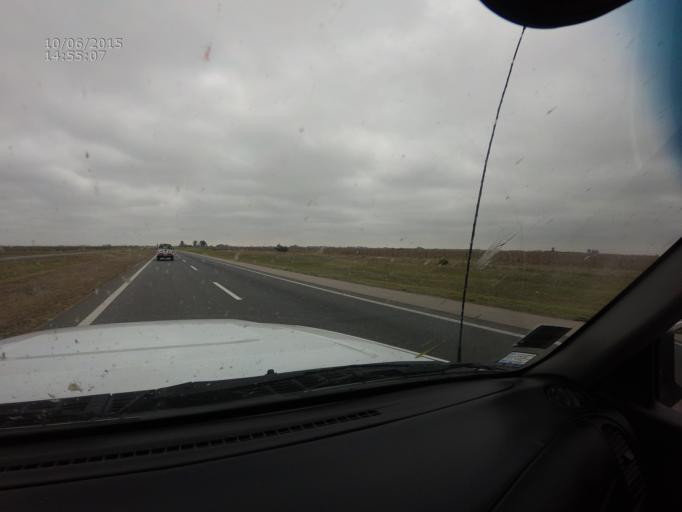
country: AR
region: Cordoba
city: Oncativo
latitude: -31.8442
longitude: -63.6933
